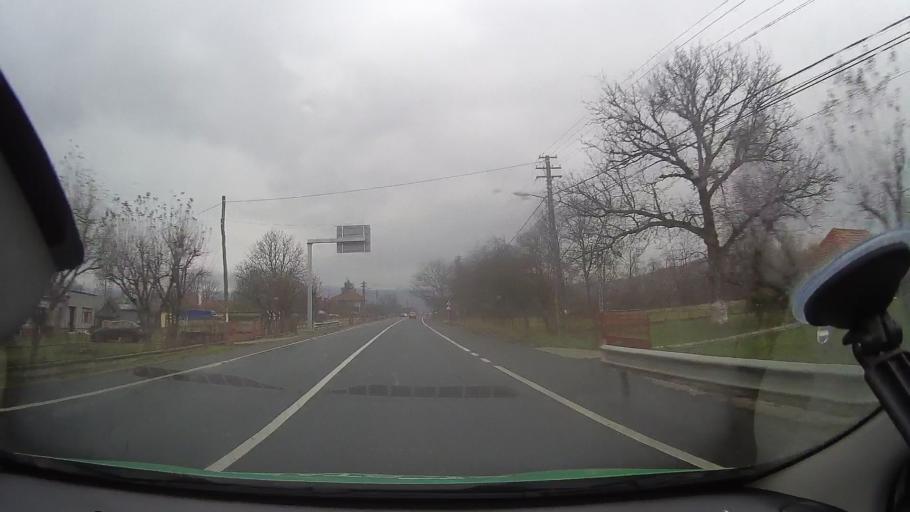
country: RO
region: Hunedoara
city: Vata de Jos
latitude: 46.1903
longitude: 22.6175
